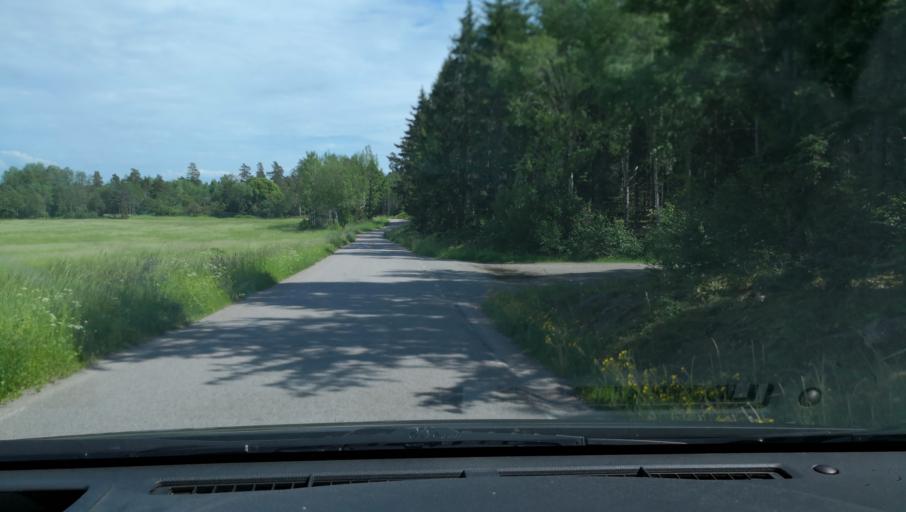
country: SE
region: Uppsala
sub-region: Uppsala Kommun
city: Alsike
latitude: 59.7054
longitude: 17.6634
